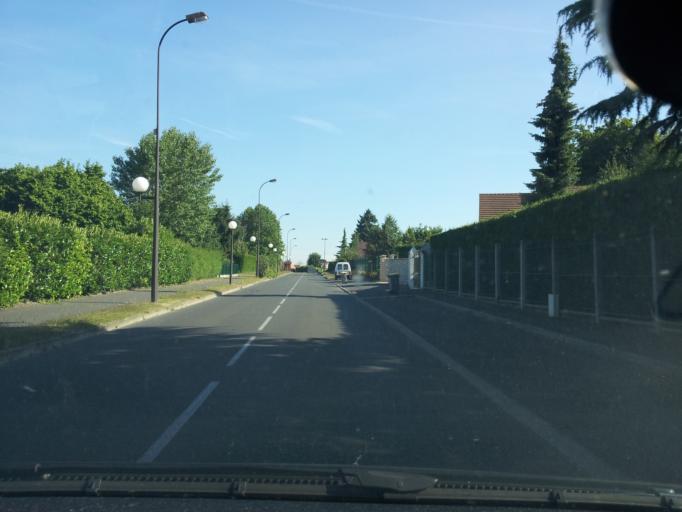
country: FR
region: Ile-de-France
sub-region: Departement de l'Essonne
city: Saint-Vrain
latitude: 48.5414
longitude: 2.3239
